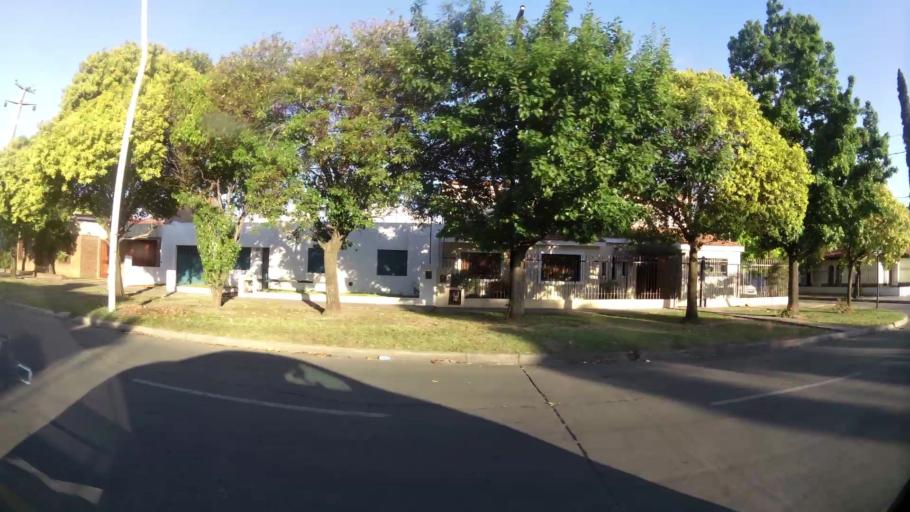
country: AR
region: Cordoba
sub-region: Departamento de Capital
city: Cordoba
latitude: -31.3788
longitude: -64.2147
